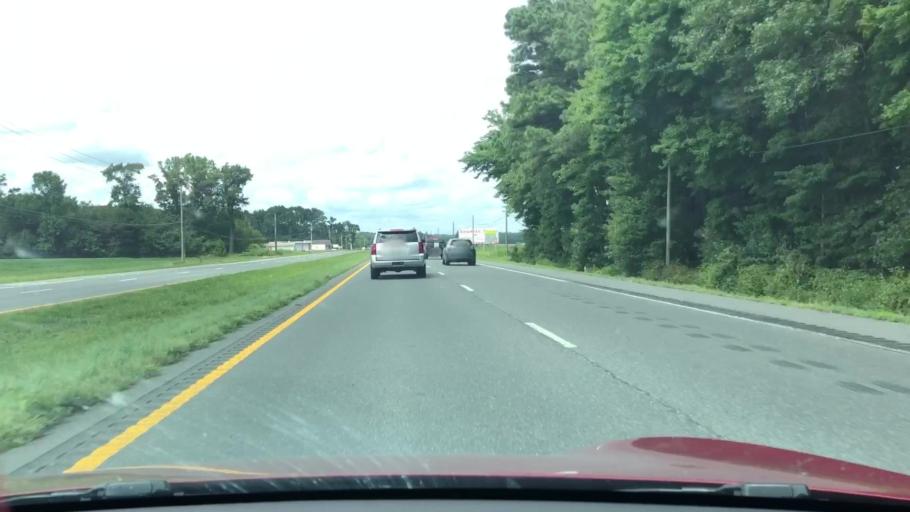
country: US
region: Virginia
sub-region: Accomack County
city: Wattsville
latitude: 37.9045
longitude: -75.5489
